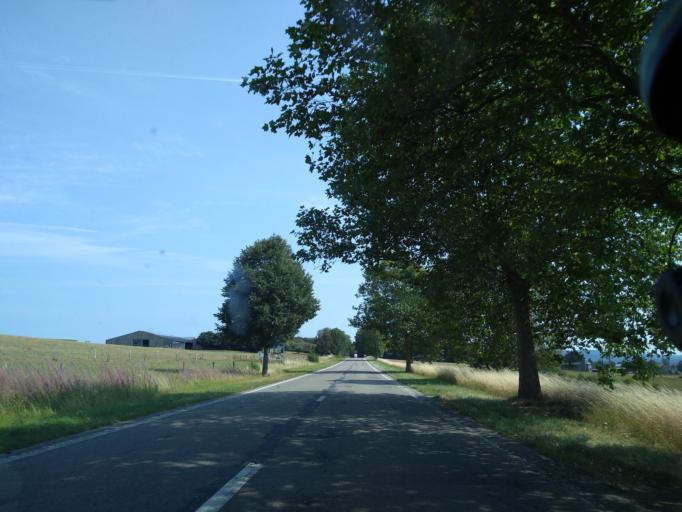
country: BE
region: Wallonia
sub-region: Province du Luxembourg
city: La Roche-en-Ardenne
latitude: 50.1656
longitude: 5.5420
